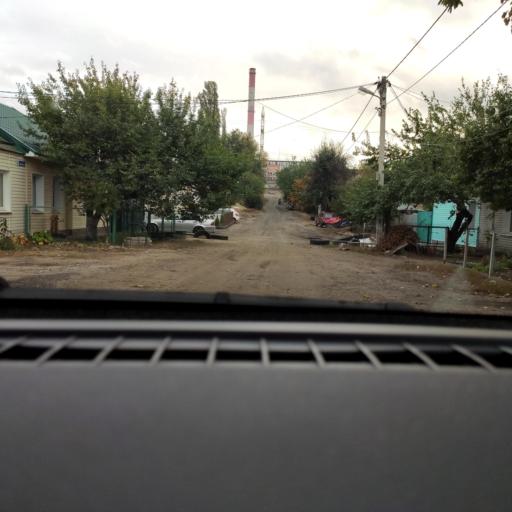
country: RU
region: Voronezj
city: Voronezh
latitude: 51.6913
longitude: 39.1552
